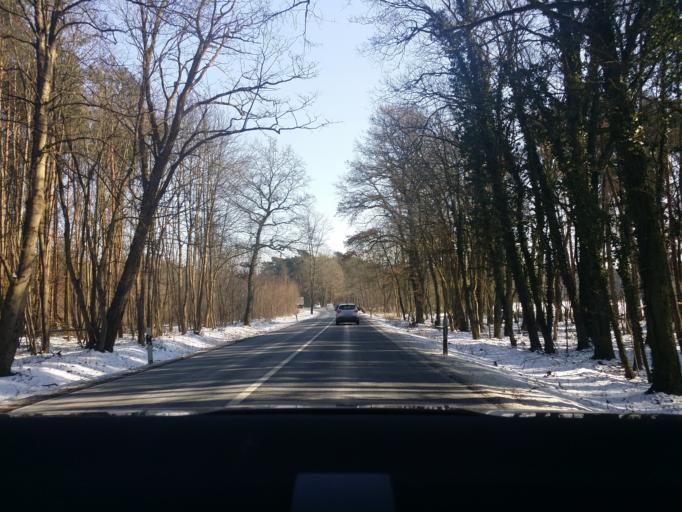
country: DE
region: Brandenburg
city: Heiligengrabe
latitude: 53.1377
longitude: 12.2722
